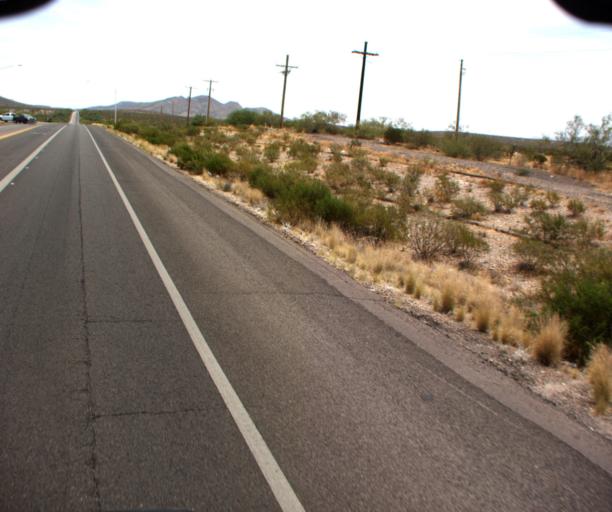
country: US
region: Arizona
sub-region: Gila County
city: Peridot
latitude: 33.2919
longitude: -110.4282
